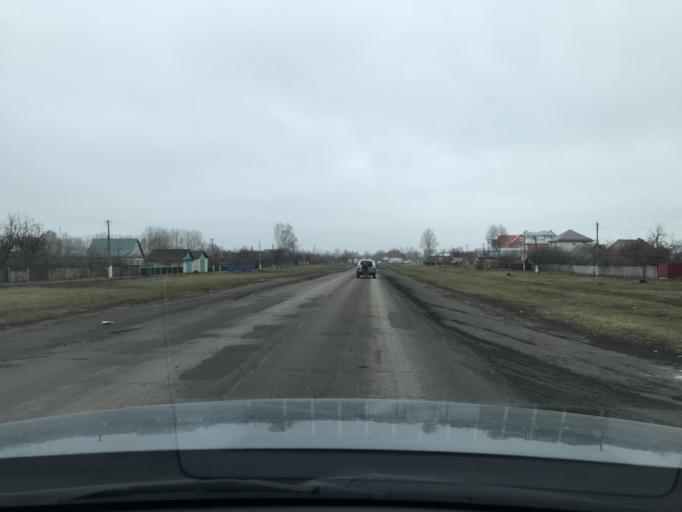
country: RU
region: Penza
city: Zemetchino
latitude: 53.5038
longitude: 42.6333
